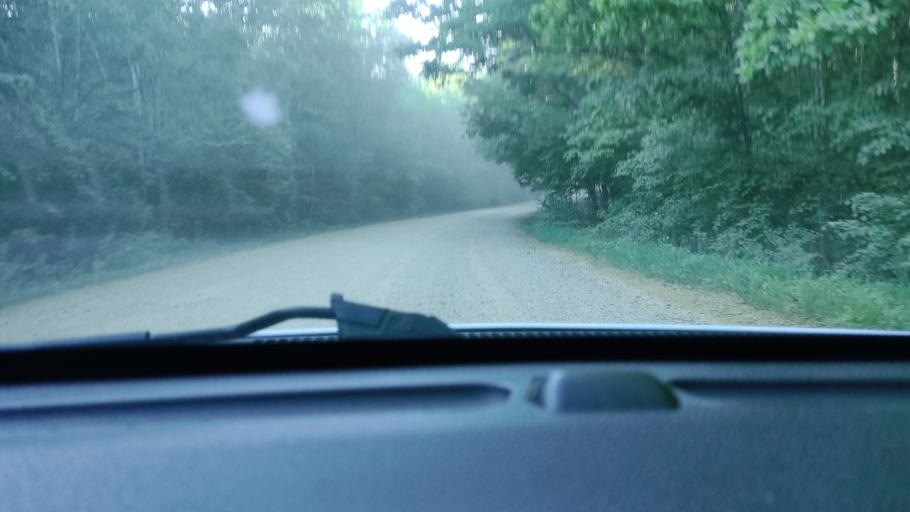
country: RU
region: Krasnodarskiy
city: Goryachiy Klyuch
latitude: 44.7132
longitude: 38.9912
